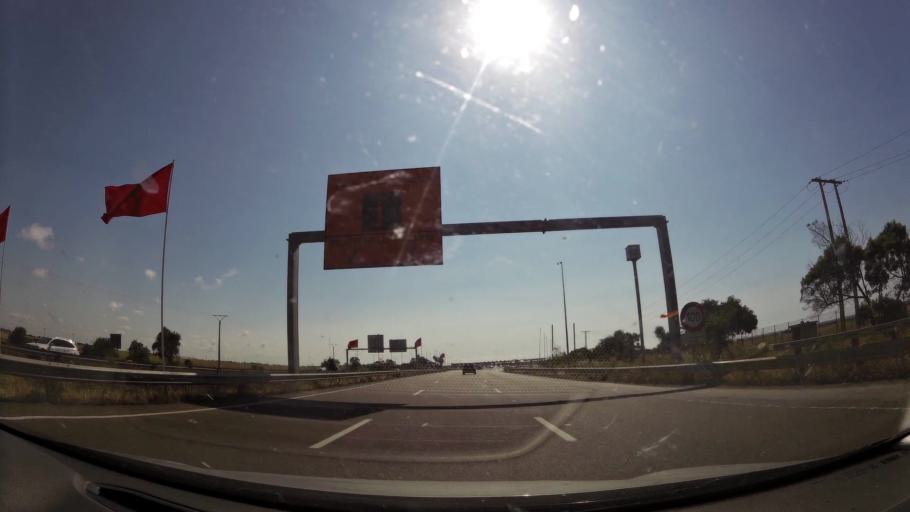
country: MA
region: Chaouia-Ouardigha
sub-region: Benslimane
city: Bouznika
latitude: 33.7988
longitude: -7.1672
